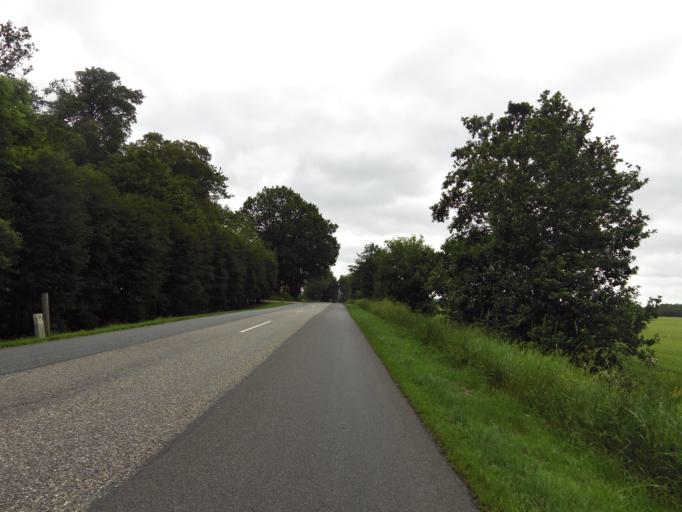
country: DK
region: South Denmark
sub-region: Tonder Kommune
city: Toftlund
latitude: 55.1524
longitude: 9.0413
